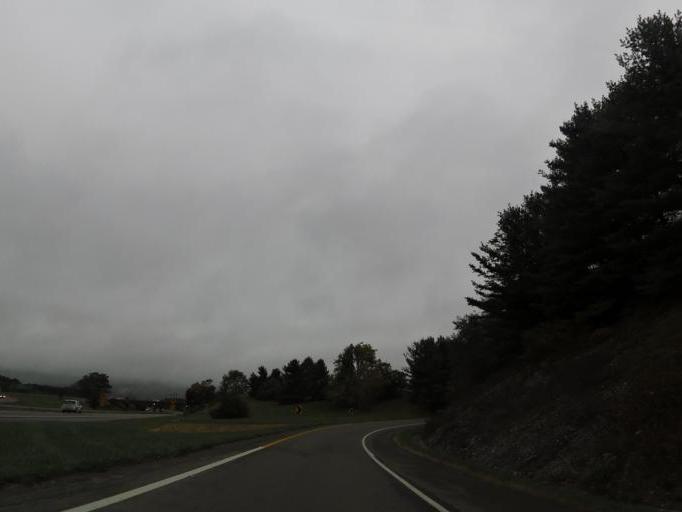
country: US
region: Virginia
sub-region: Wythe County
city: Wytheville
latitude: 36.9641
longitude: -81.0658
